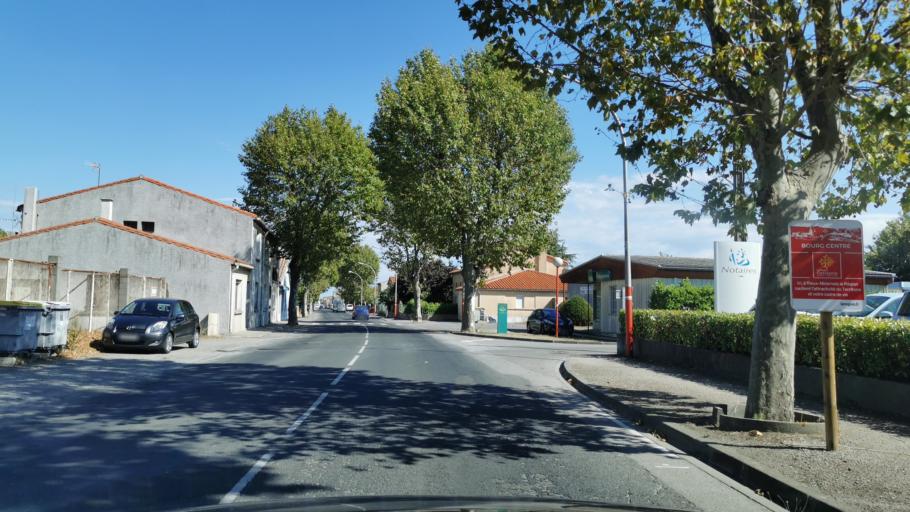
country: FR
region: Languedoc-Roussillon
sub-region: Departement de l'Aude
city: Rieux-Minervois
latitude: 43.2838
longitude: 2.5768
